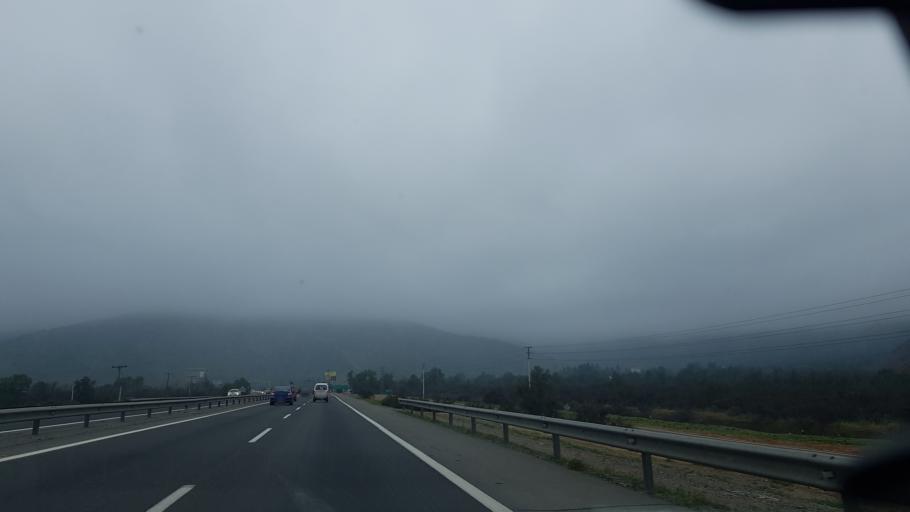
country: CL
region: Santiago Metropolitan
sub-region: Provincia de Talagante
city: Penaflor
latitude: -33.4575
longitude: -70.9172
